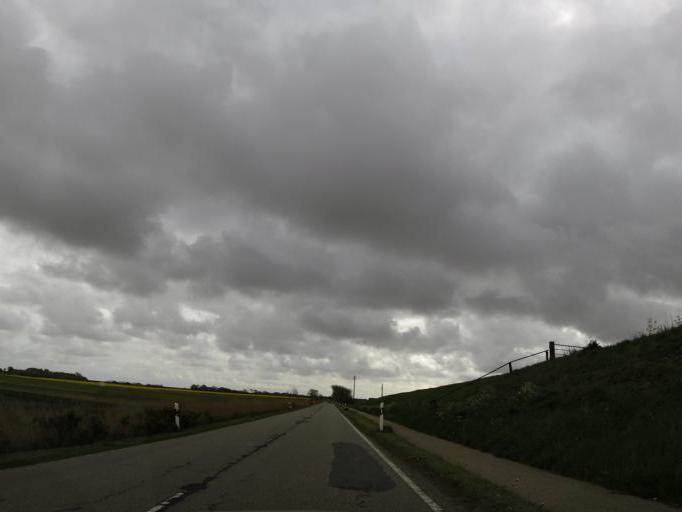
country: DE
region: Schleswig-Holstein
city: Dagebull
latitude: 54.7406
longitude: 8.7242
